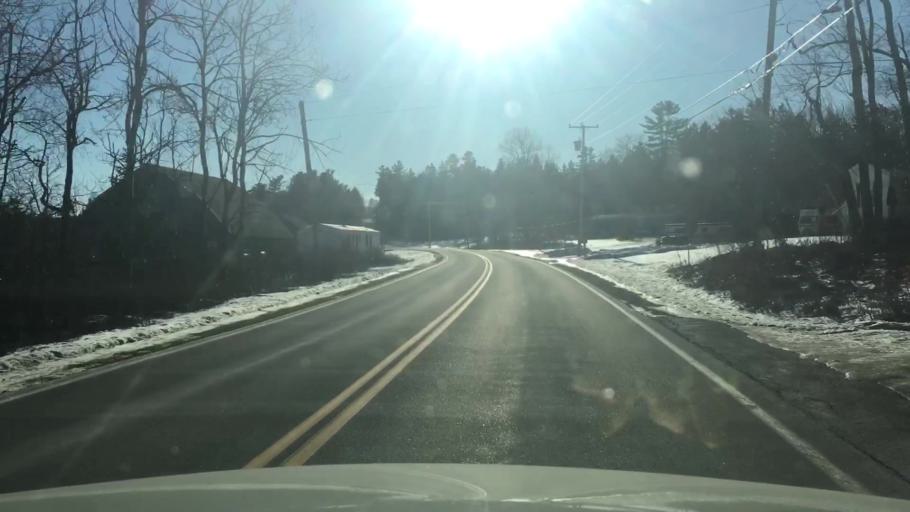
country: US
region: Maine
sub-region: Hancock County
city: Orland
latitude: 44.5202
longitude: -68.7490
